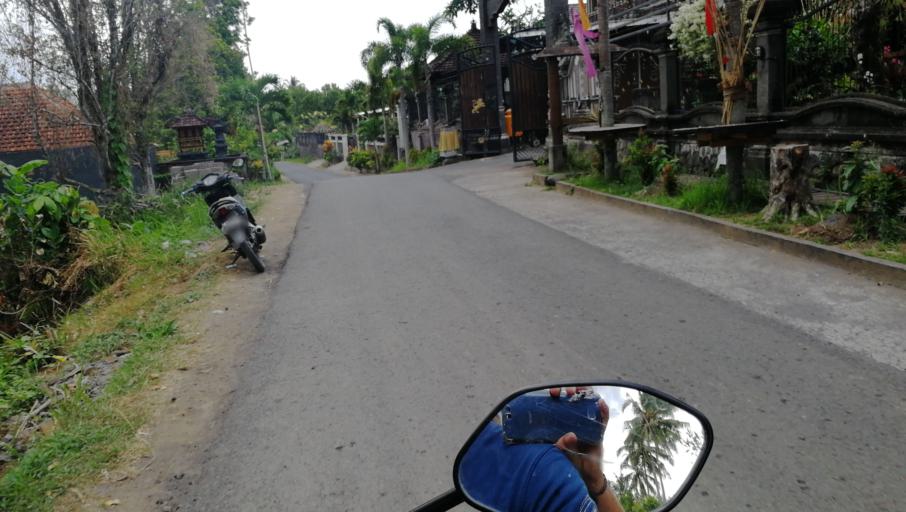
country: ID
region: Bali
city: Puspajati
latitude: -8.2715
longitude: 115.0139
